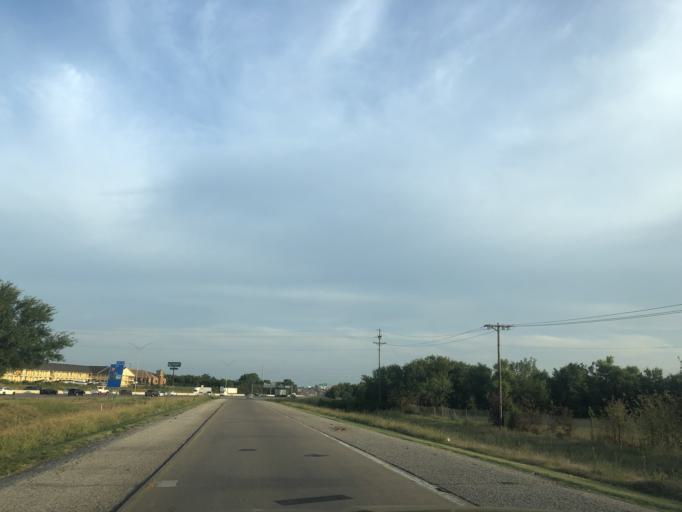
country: US
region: Texas
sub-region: Dallas County
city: Mesquite
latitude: 32.7807
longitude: -96.6253
